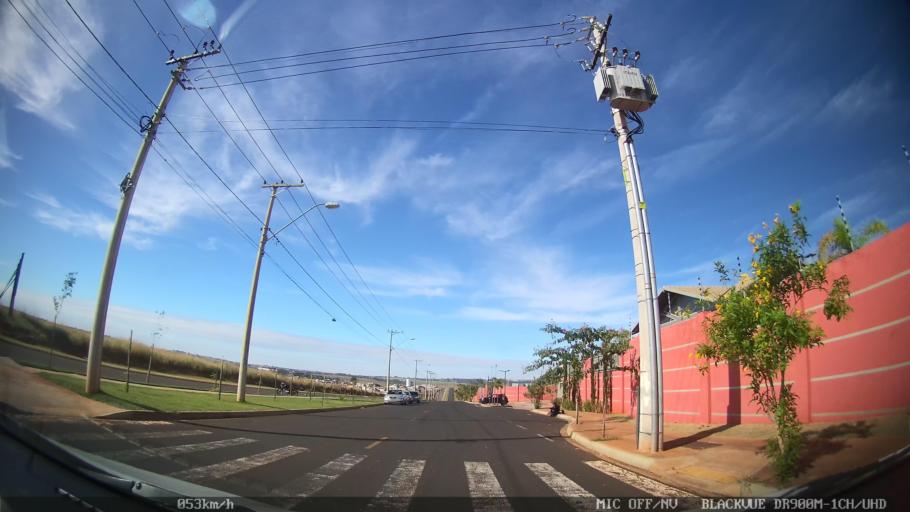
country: BR
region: Sao Paulo
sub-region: Sao Jose Do Rio Preto
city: Sao Jose do Rio Preto
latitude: -20.8058
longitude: -49.3282
